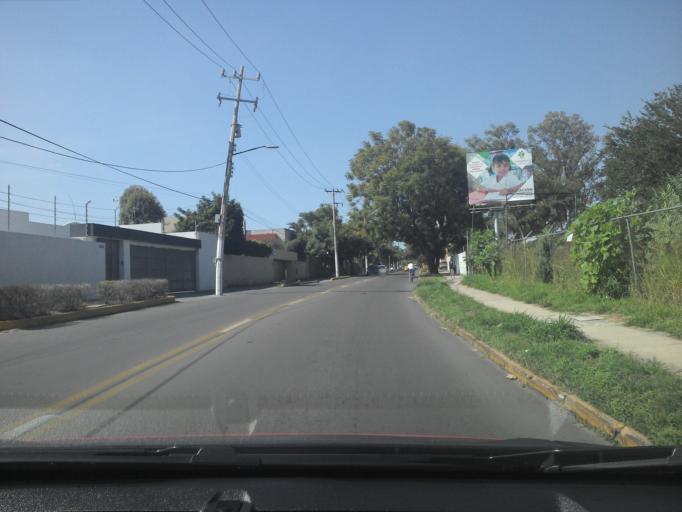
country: MX
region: Jalisco
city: Zapopan2
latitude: 20.6919
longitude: -103.4060
